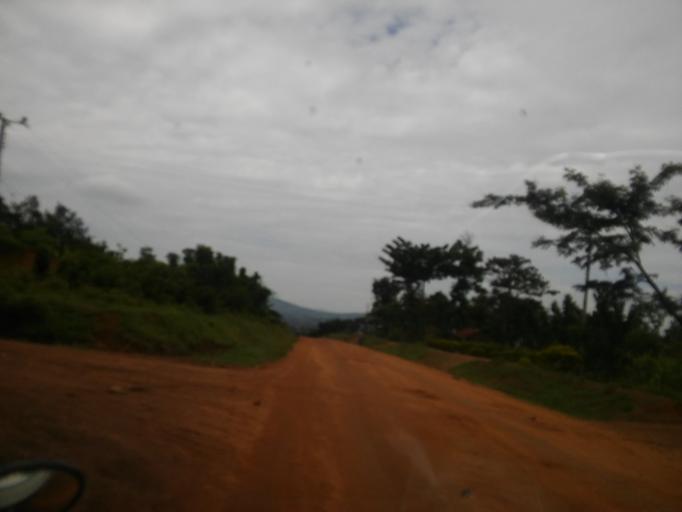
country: UG
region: Eastern Region
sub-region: Mbale District
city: Mbale
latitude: 0.9680
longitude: 34.2088
